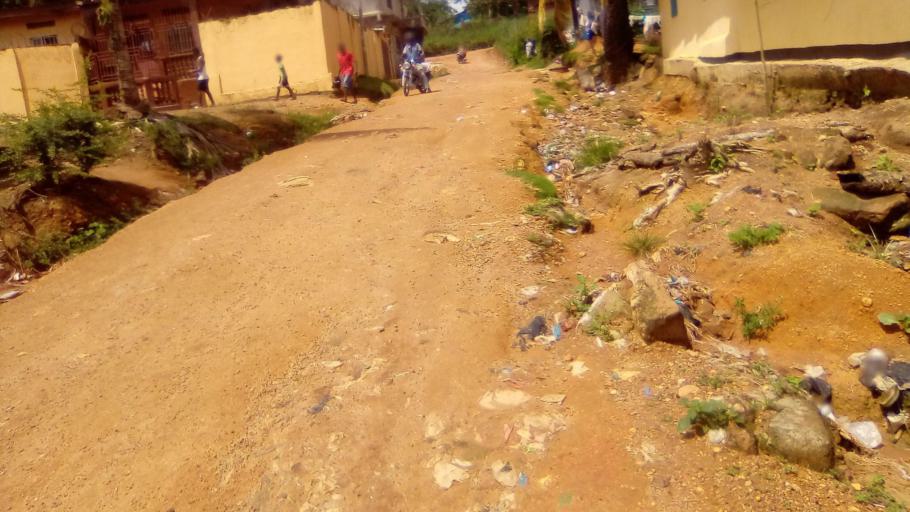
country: SL
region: Southern Province
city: Bo
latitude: 7.9782
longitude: -11.7410
